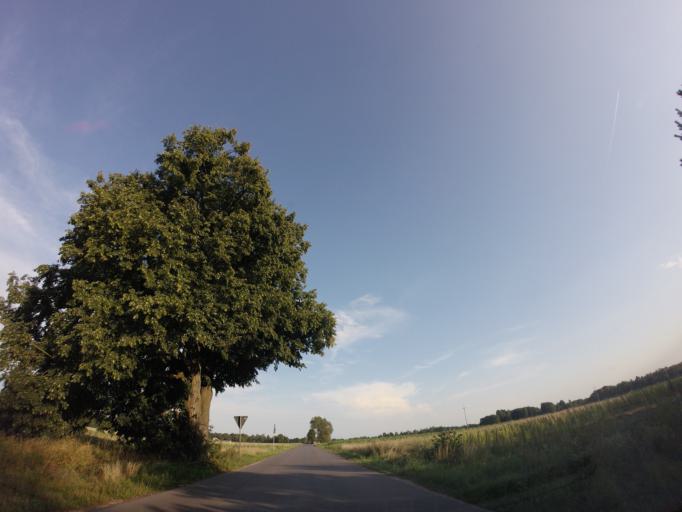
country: PL
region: Lublin Voivodeship
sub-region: Powiat pulawski
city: Kurow
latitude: 51.4303
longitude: 22.2160
